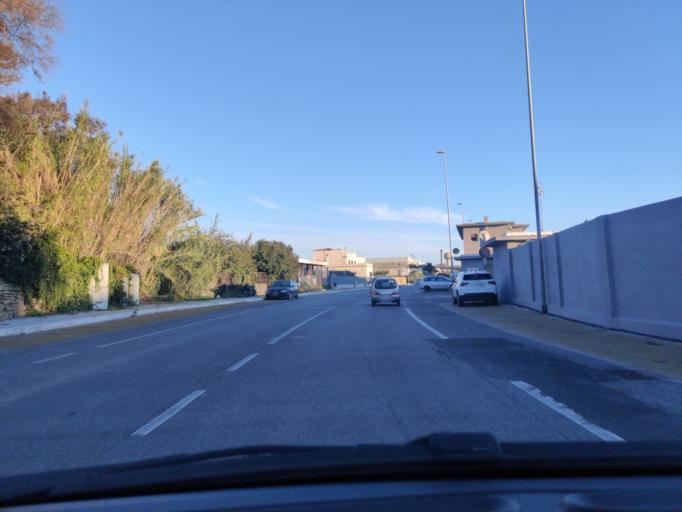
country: IT
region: Latium
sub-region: Citta metropolitana di Roma Capitale
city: Civitavecchia
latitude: 42.1073
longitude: 11.7811
